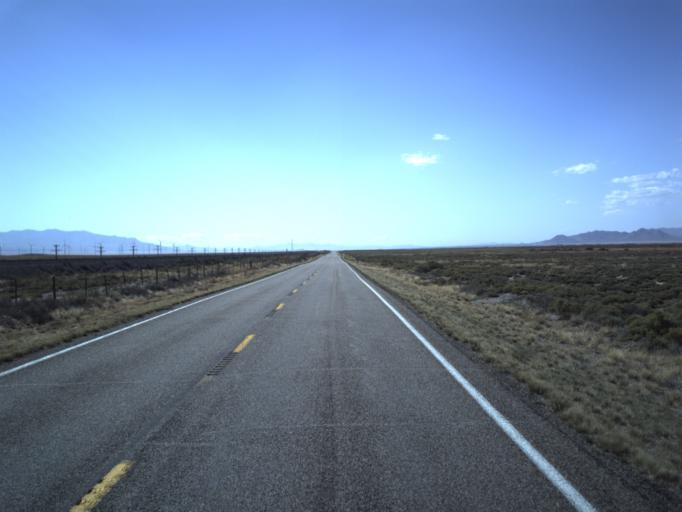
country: US
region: Utah
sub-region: Beaver County
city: Milford
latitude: 38.6434
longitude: -112.9831
